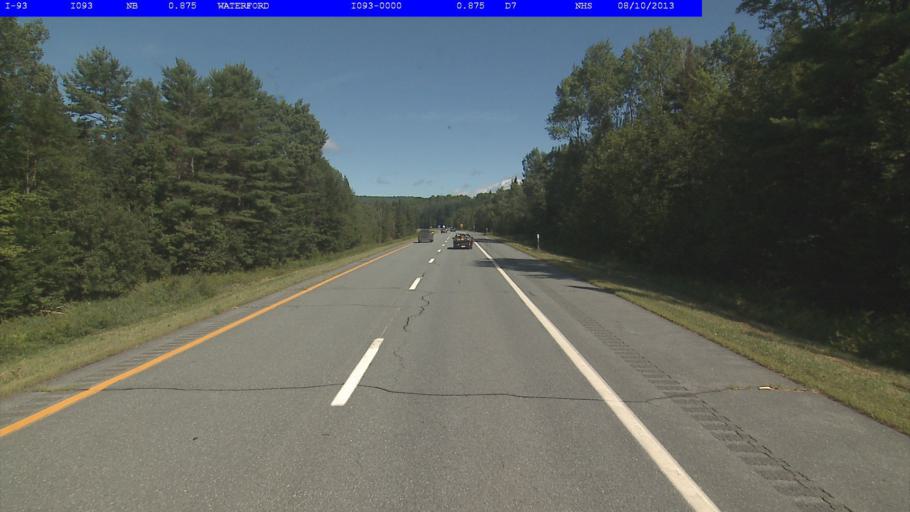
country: US
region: New Hampshire
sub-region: Grafton County
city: Littleton
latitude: 44.3554
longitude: -71.8956
